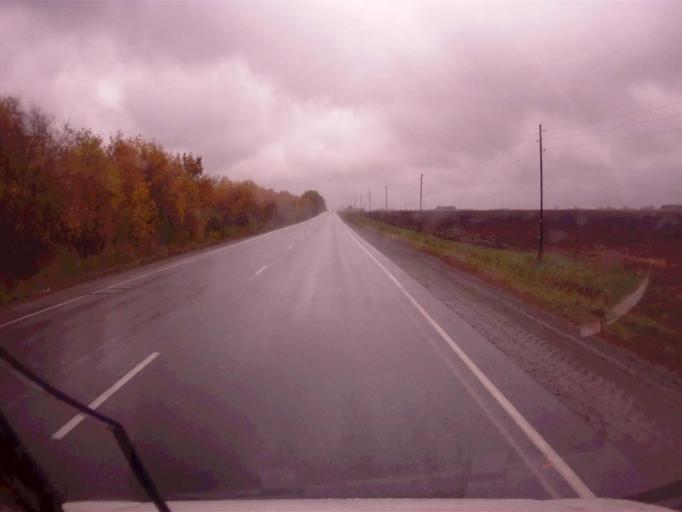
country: RU
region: Chelyabinsk
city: Argayash
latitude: 55.4269
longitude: 61.0000
